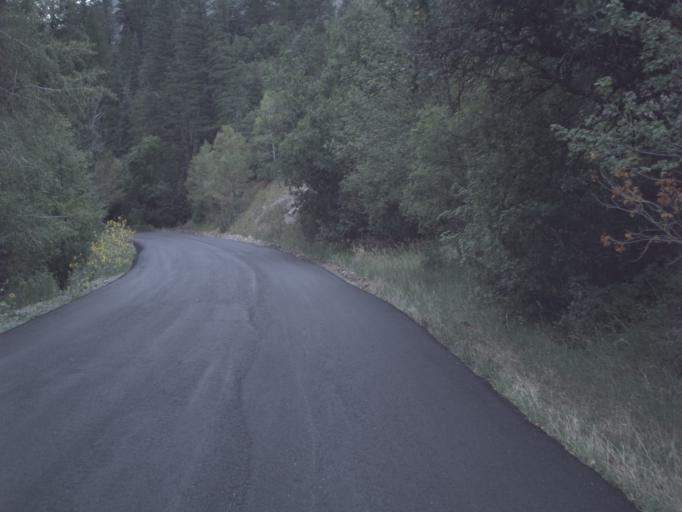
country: US
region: Utah
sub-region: Utah County
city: Cedar Hills
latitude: 40.4496
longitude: -111.6473
